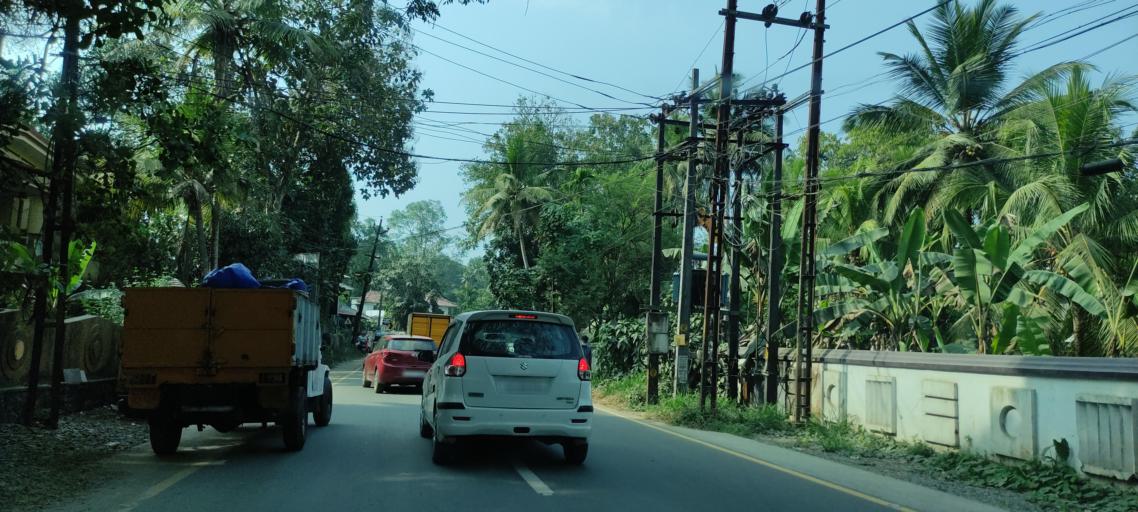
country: IN
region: Kerala
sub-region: Pattanamtitta
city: Tiruvalla
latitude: 9.3671
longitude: 76.5438
